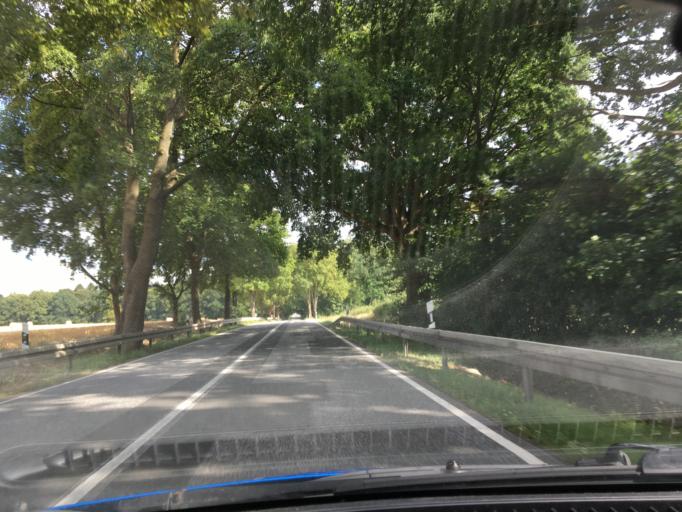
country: DE
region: Mecklenburg-Vorpommern
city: Lubtheen
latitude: 53.3903
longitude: 11.0580
